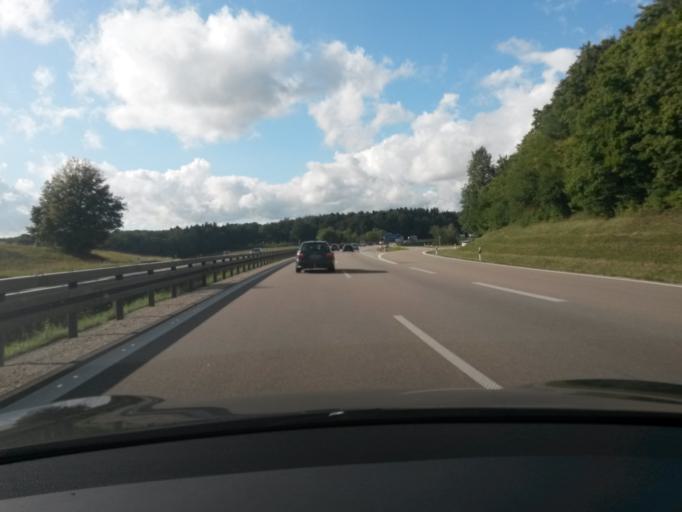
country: DE
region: Bavaria
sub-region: Upper Palatinate
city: Brunn
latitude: 49.0876
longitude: 11.8908
